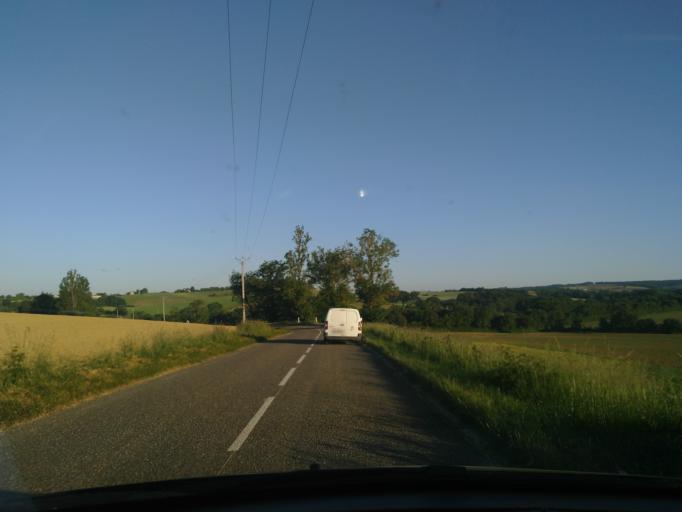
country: FR
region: Midi-Pyrenees
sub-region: Departement du Gers
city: Valence-sur-Baise
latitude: 43.8712
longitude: 0.4822
